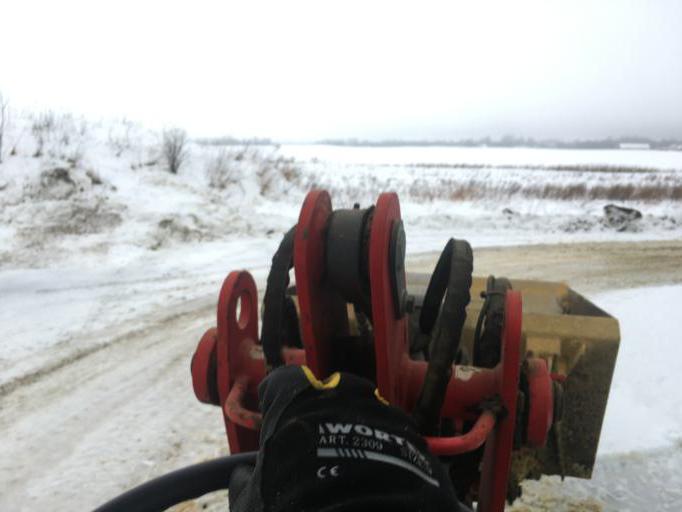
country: EE
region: Jaervamaa
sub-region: Jaerva-Jaani vald
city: Jarva-Jaani
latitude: 59.1498
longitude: 25.7348
